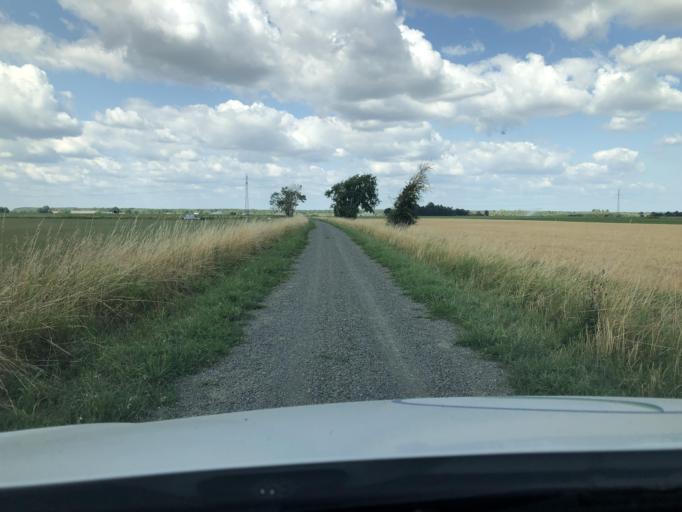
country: SE
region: Skane
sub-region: Kristianstads Kommun
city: Degeberga
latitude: 55.8815
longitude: 14.0817
